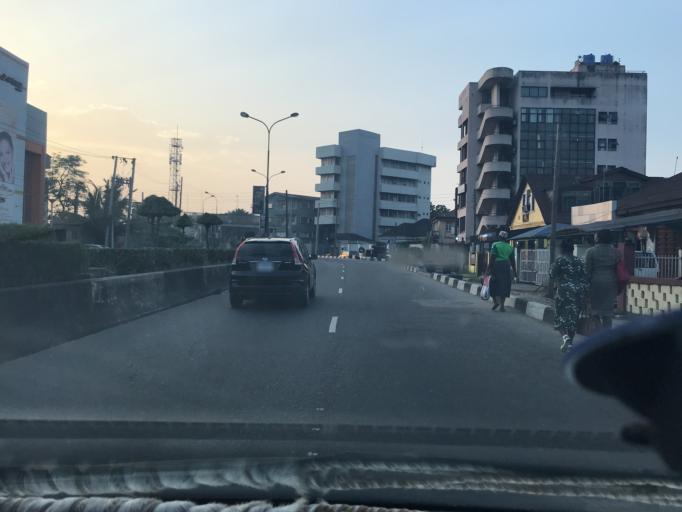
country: NG
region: Lagos
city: Makoko
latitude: 6.4982
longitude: 3.3787
